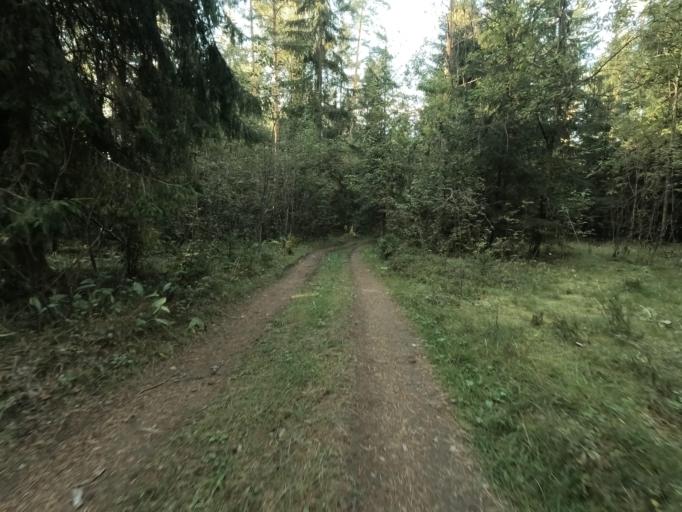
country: RU
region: Leningrad
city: Imeni Sverdlova
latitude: 59.8415
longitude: 30.7297
